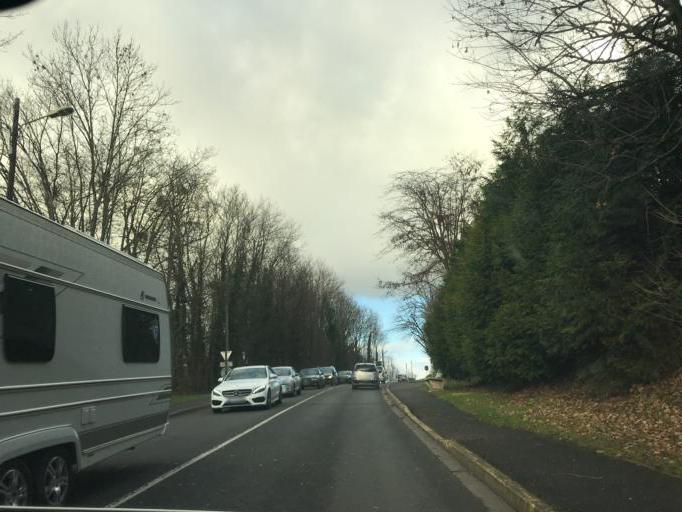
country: FR
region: Ile-de-France
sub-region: Departement de Seine-et-Marne
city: Claye-Souilly
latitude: 48.9467
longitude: 2.6904
